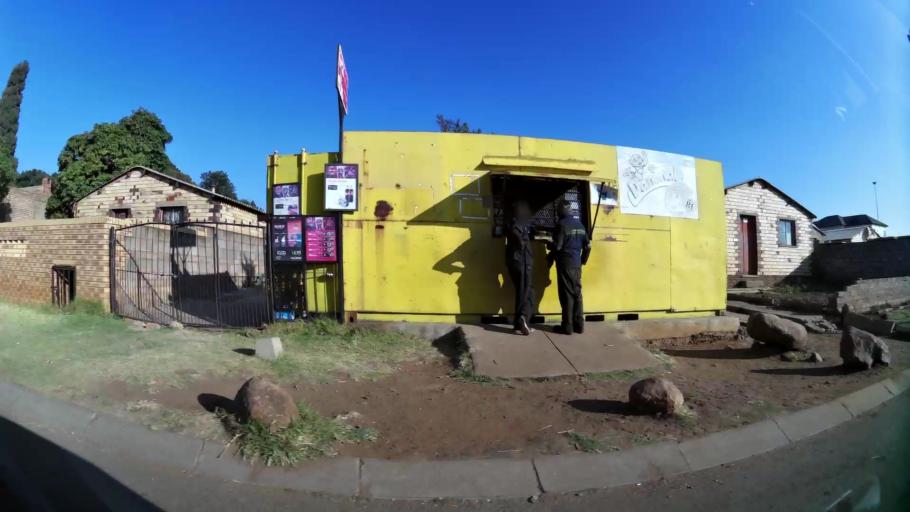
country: ZA
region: Gauteng
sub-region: City of Johannesburg Metropolitan Municipality
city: Soweto
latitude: -26.2676
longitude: 27.8700
